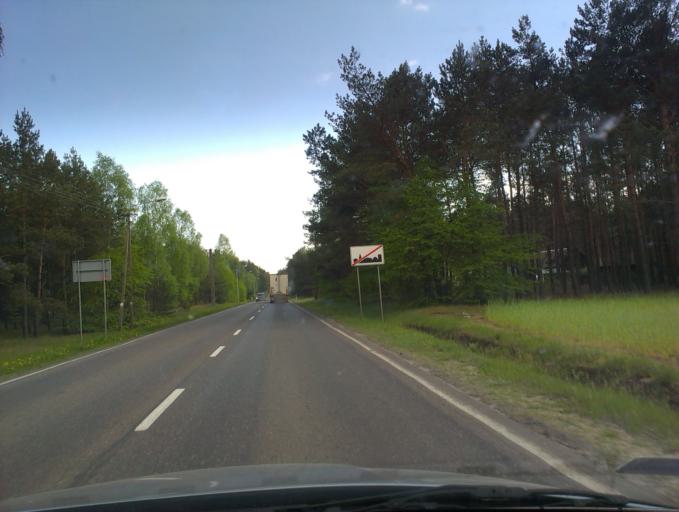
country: PL
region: Kujawsko-Pomorskie
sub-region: Powiat tucholski
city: Cekcyn
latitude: 53.5277
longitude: 17.9474
